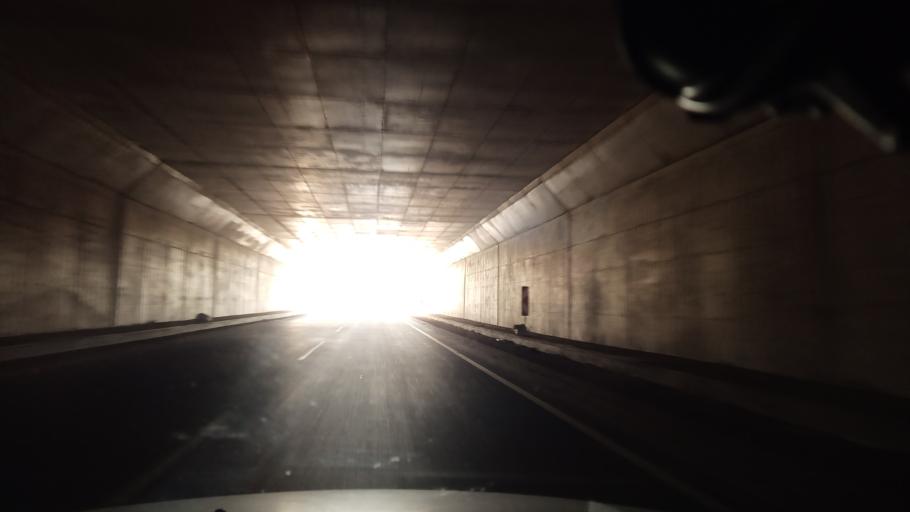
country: TR
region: Sakarya
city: Adapazari
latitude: 40.8393
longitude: 30.3662
